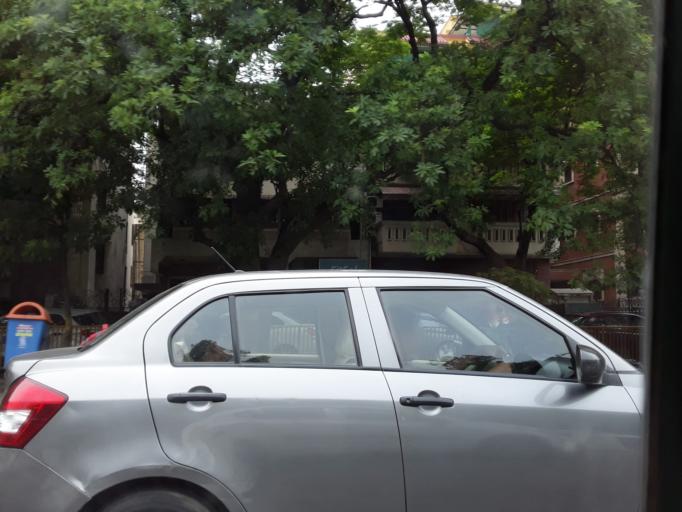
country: IN
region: NCT
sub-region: New Delhi
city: New Delhi
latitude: 28.5432
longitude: 77.2311
